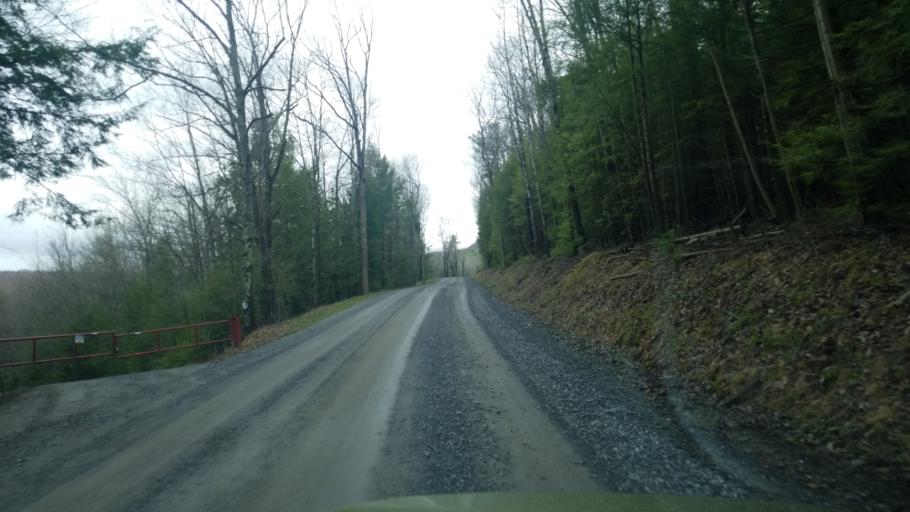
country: US
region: Pennsylvania
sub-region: Clearfield County
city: Shiloh
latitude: 41.1187
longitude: -78.3412
